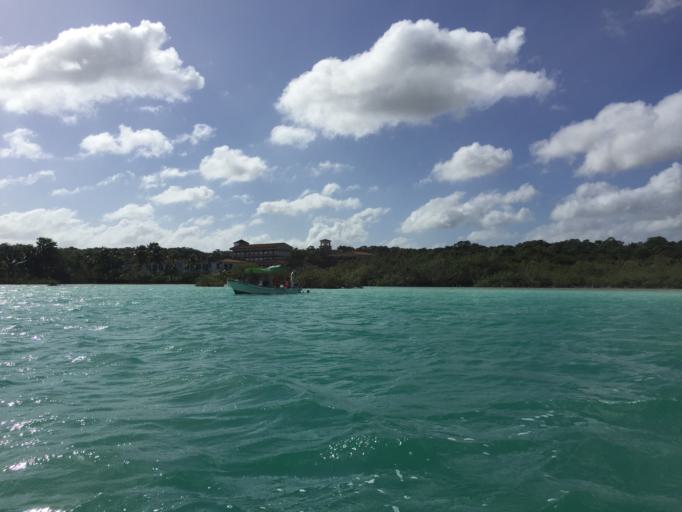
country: MX
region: Quintana Roo
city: Bacalar
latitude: 18.6355
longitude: -88.4099
